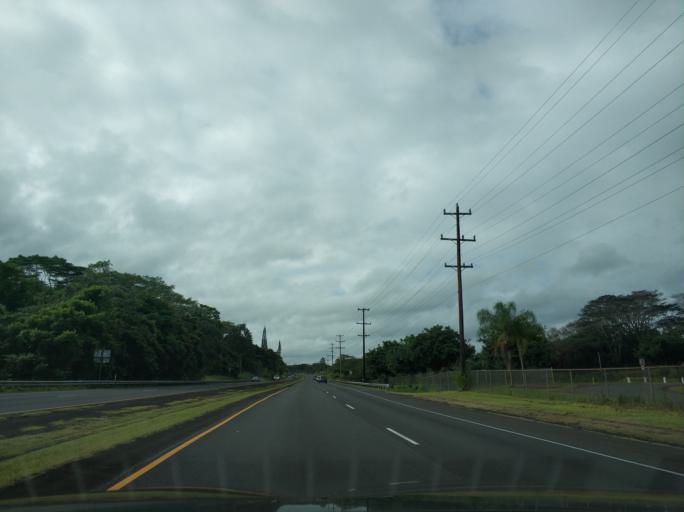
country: US
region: Hawaii
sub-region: Hawaii County
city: Kea'au
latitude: 19.6221
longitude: -155.0414
